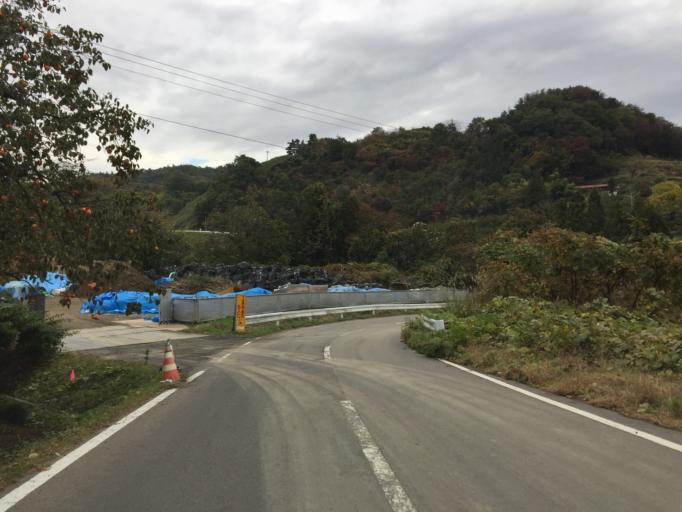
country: JP
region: Fukushima
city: Fukushima-shi
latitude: 37.8349
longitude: 140.4380
